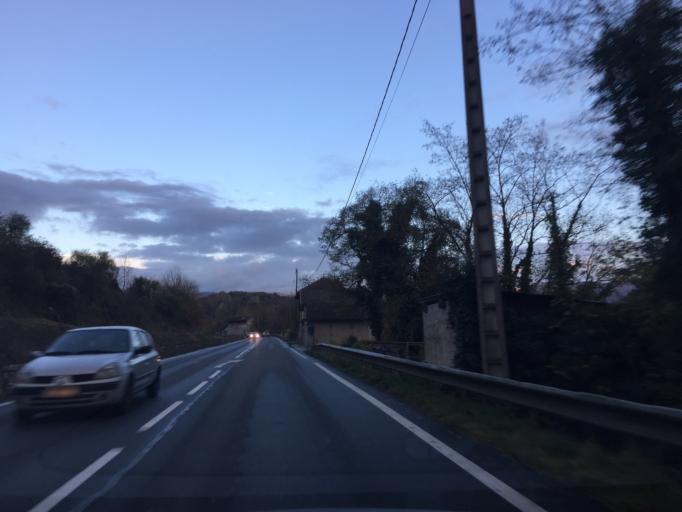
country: FR
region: Rhone-Alpes
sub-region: Departement de l'Isere
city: Saint-Just-de-Claix
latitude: 45.0623
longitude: 5.2614
